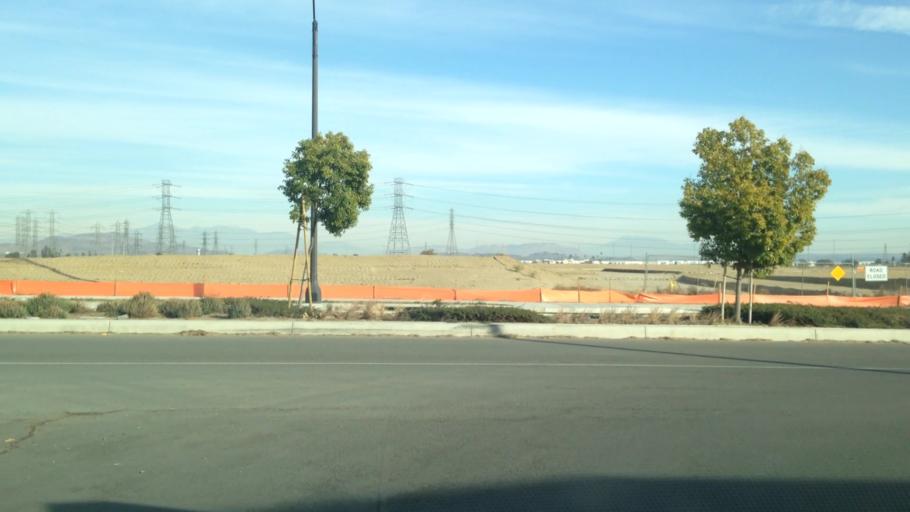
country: US
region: California
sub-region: Riverside County
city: Mira Loma
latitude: 34.0029
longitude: -117.5761
